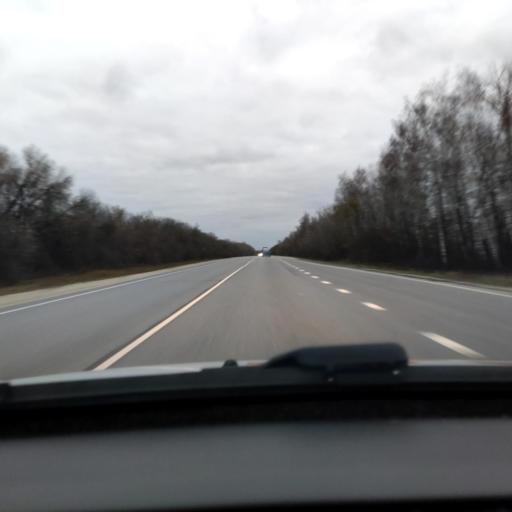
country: RU
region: Lipetsk
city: Borinskoye
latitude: 52.4083
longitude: 39.2444
